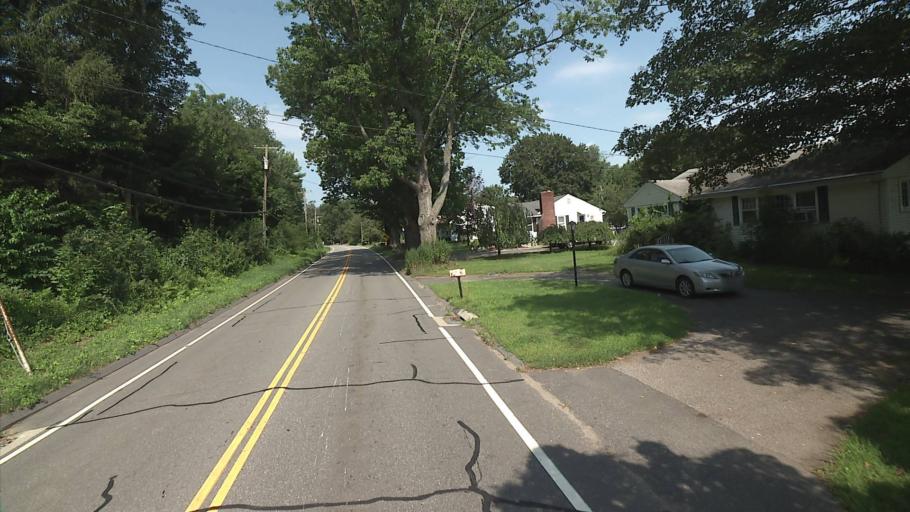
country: US
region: Connecticut
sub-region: New London County
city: Baltic
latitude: 41.5666
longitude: -72.1453
